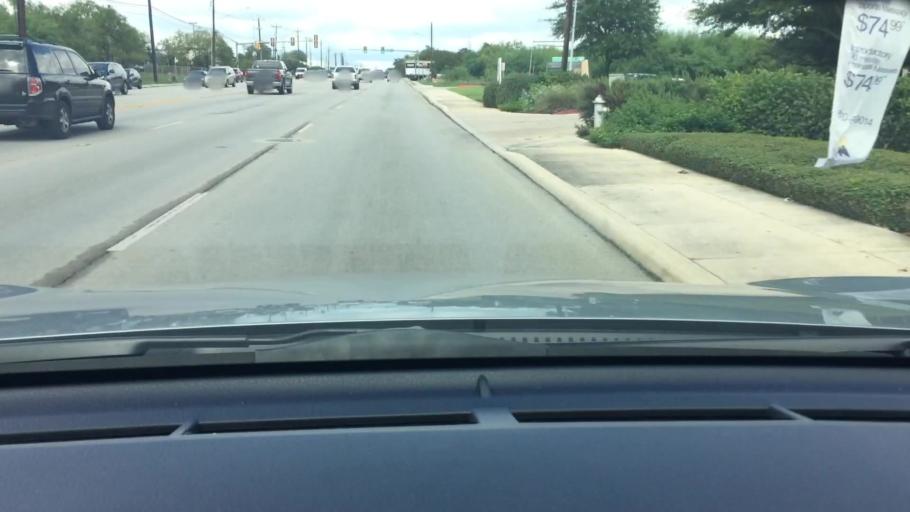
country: US
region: Texas
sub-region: Bexar County
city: Leon Valley
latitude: 29.5350
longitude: -98.5886
